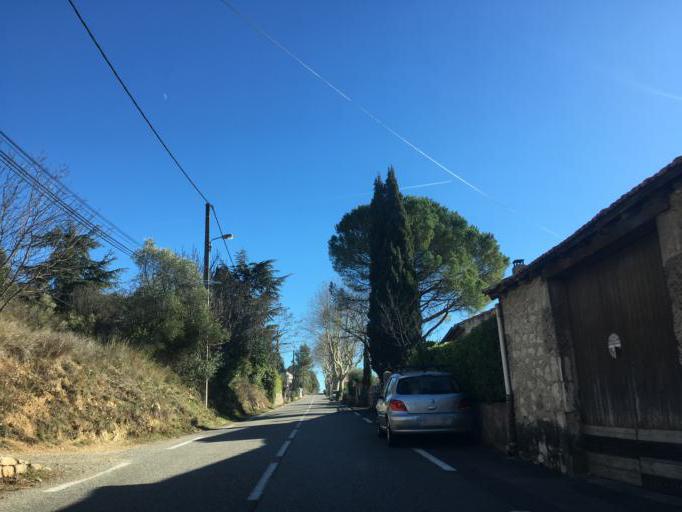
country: FR
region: Provence-Alpes-Cote d'Azur
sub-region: Departement du Var
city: Barjols
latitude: 43.5968
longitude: 5.9622
